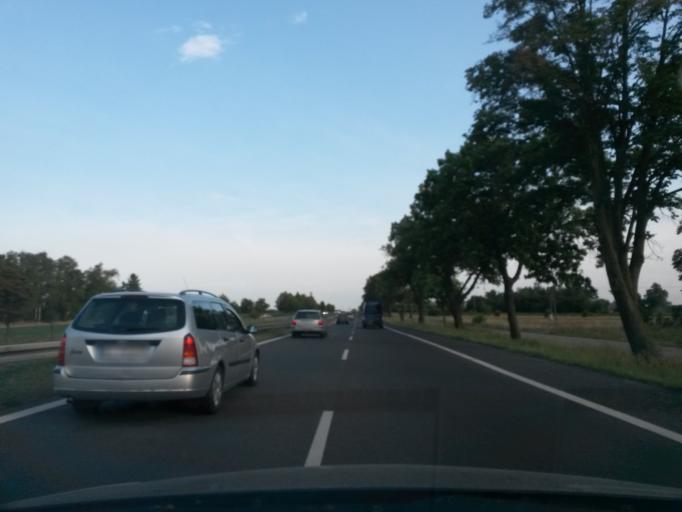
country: PL
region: Masovian Voivodeship
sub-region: Powiat plonski
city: Zaluski
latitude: 52.4937
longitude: 20.5436
